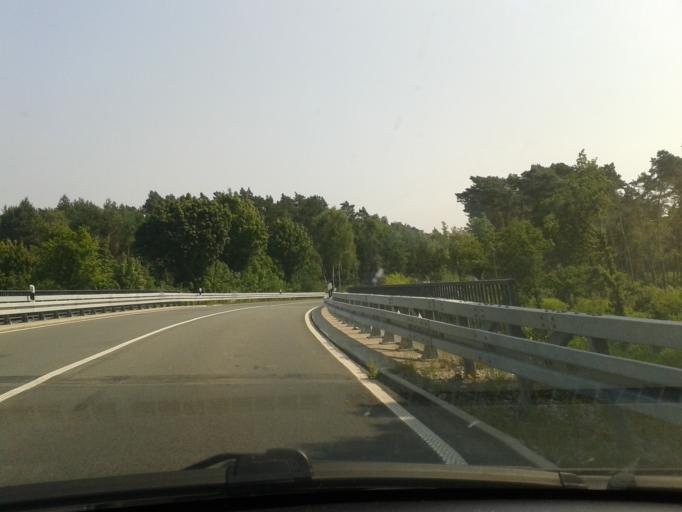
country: DE
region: North Rhine-Westphalia
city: Bad Lippspringe
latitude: 51.7795
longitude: 8.7797
